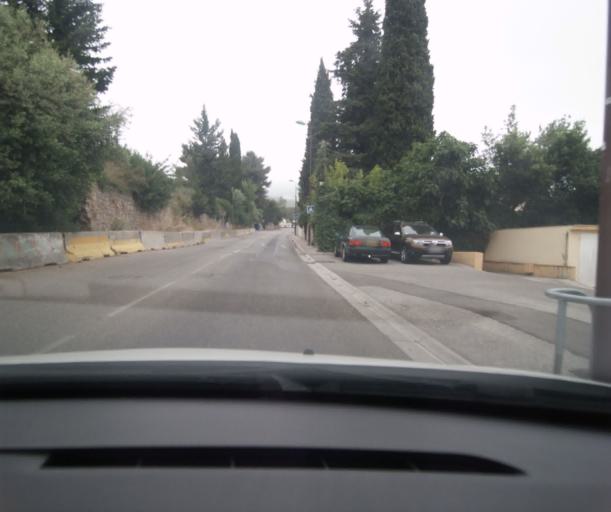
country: FR
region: Provence-Alpes-Cote d'Azur
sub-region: Departement du Var
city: La Valette-du-Var
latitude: 43.1425
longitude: 5.9796
